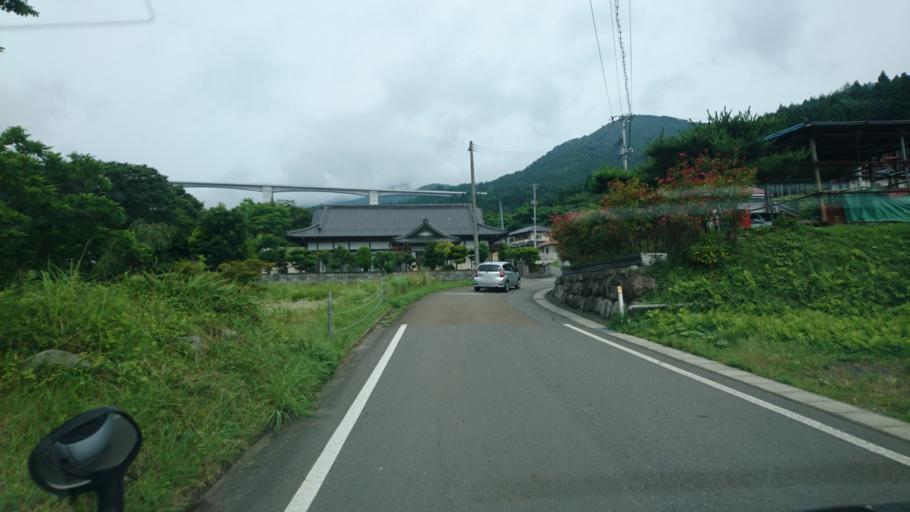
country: JP
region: Iwate
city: Ofunato
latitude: 39.1253
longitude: 141.8086
